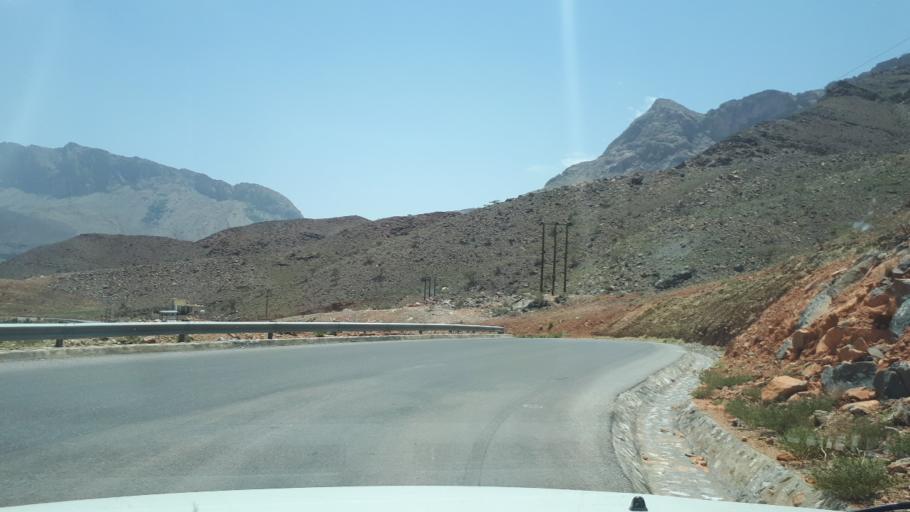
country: OM
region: Muhafazat ad Dakhiliyah
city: Bahla'
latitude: 23.1950
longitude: 57.1374
